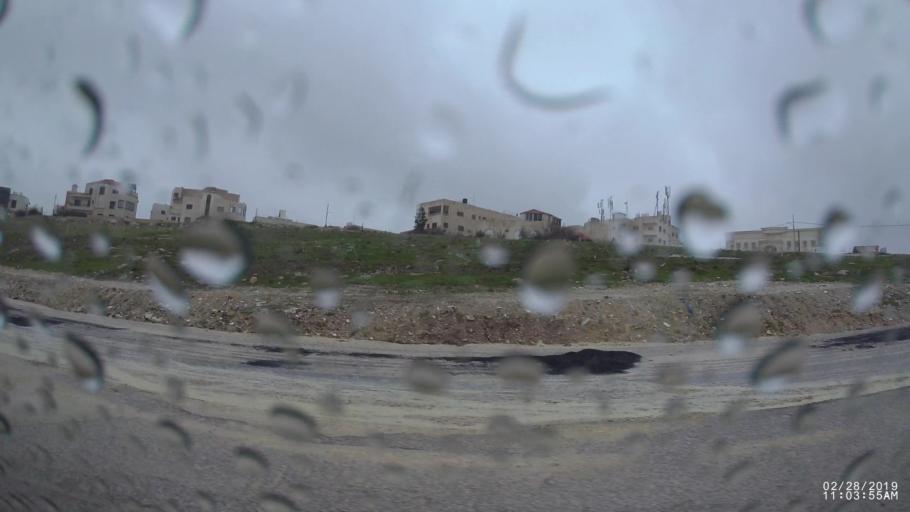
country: JO
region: Amman
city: Al Jubayhah
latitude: 32.0132
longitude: 35.8961
